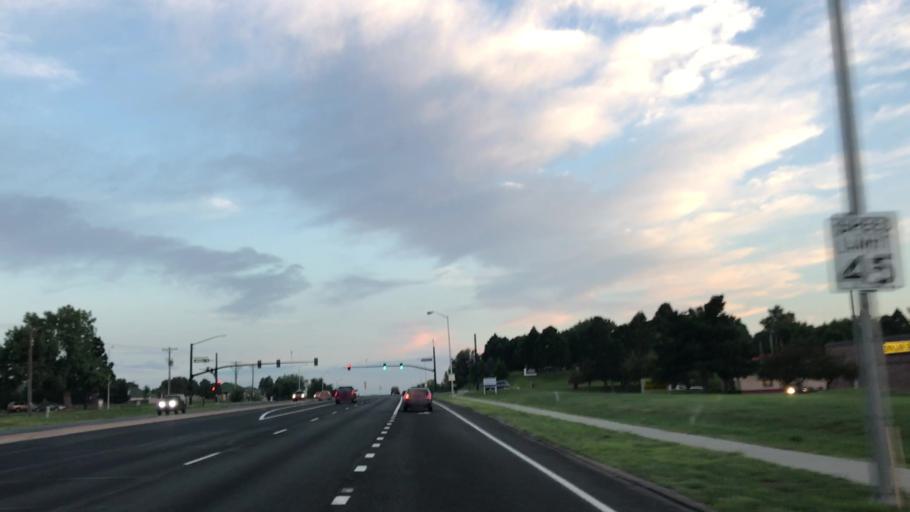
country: US
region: Colorado
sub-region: El Paso County
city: Stratmoor
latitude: 38.8076
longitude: -104.7803
